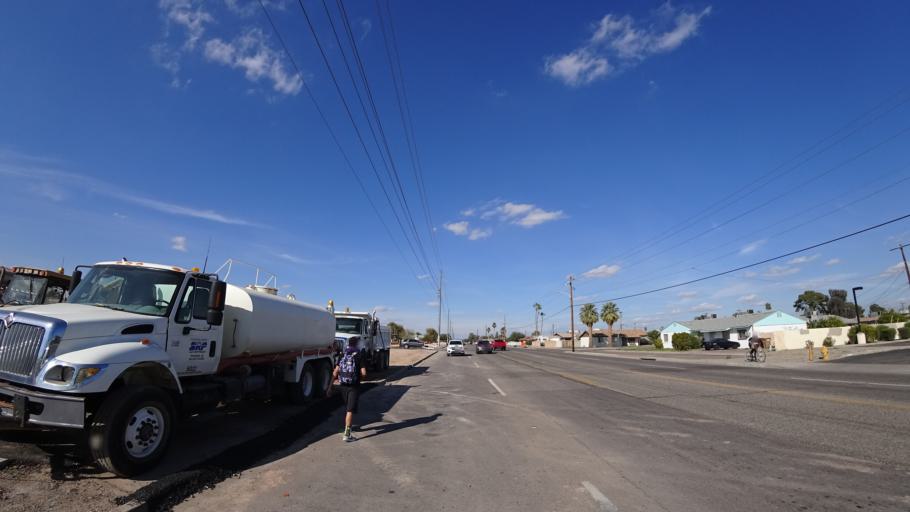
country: US
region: Arizona
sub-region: Maricopa County
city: Peoria
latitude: 33.5823
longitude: -112.2204
